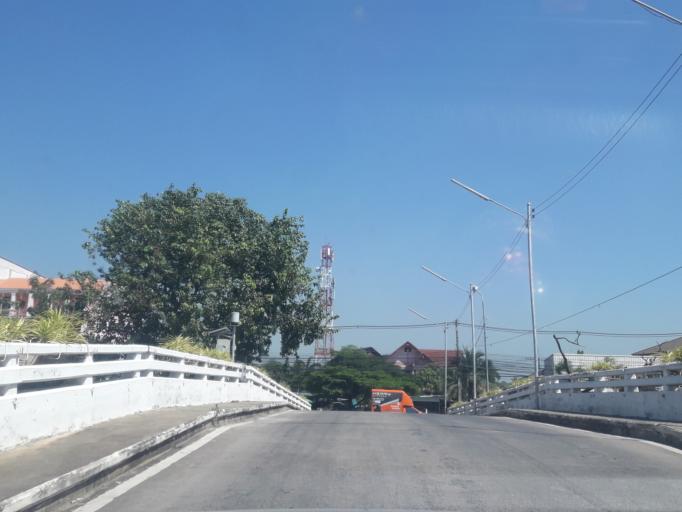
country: TH
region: Sara Buri
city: Nong Khae
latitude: 14.3346
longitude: 100.8710
